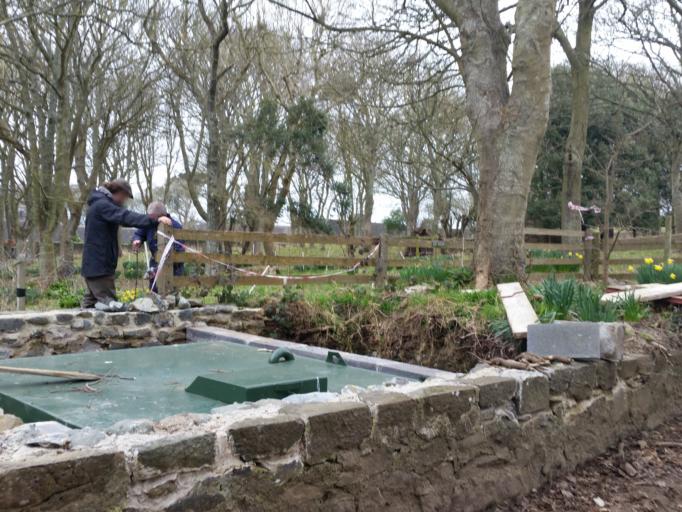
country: IE
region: Leinster
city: Portraine
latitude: 53.4914
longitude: -6.0251
